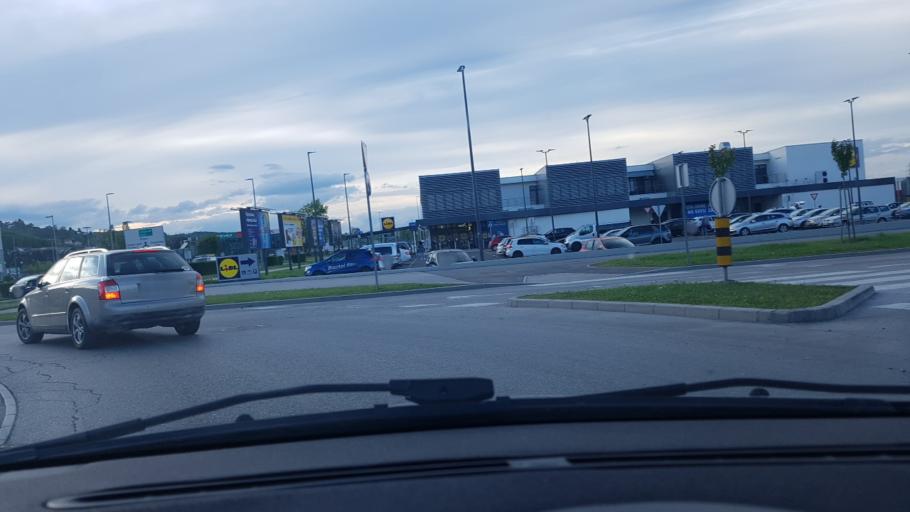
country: HR
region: Zagrebacka
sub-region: Grad Samobor
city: Samobor
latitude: 45.8089
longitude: 15.7154
